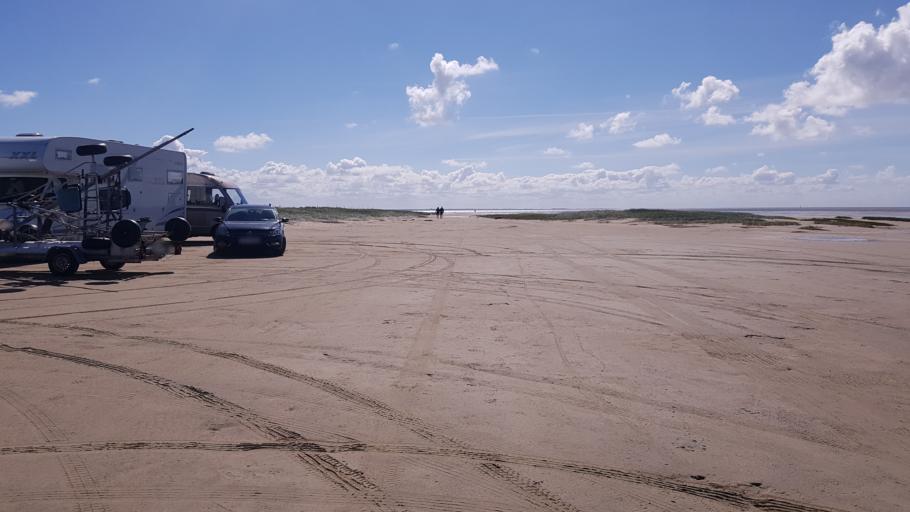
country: DE
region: Schleswig-Holstein
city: List
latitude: 55.0775
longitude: 8.5304
